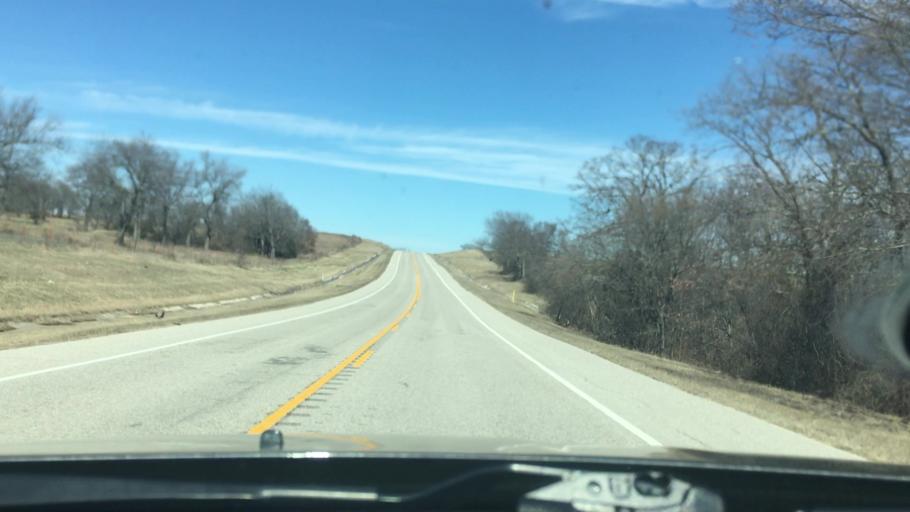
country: US
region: Oklahoma
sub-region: Carter County
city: Dickson
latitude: 34.3373
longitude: -96.9509
